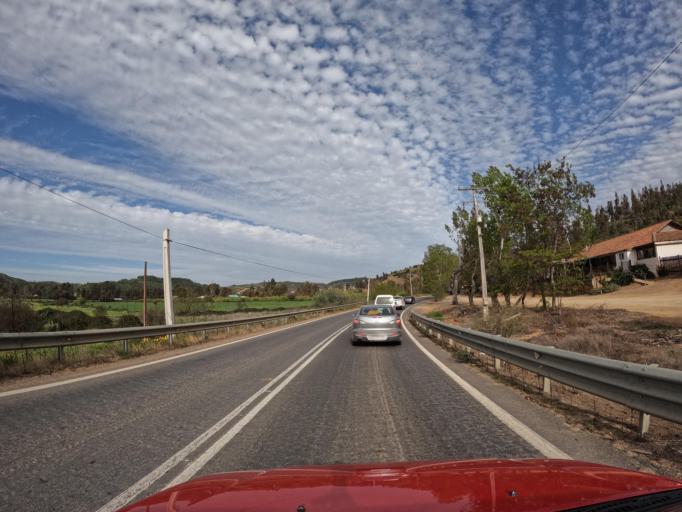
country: CL
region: O'Higgins
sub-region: Provincia de Colchagua
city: Santa Cruz
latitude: -34.3004
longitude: -71.7981
